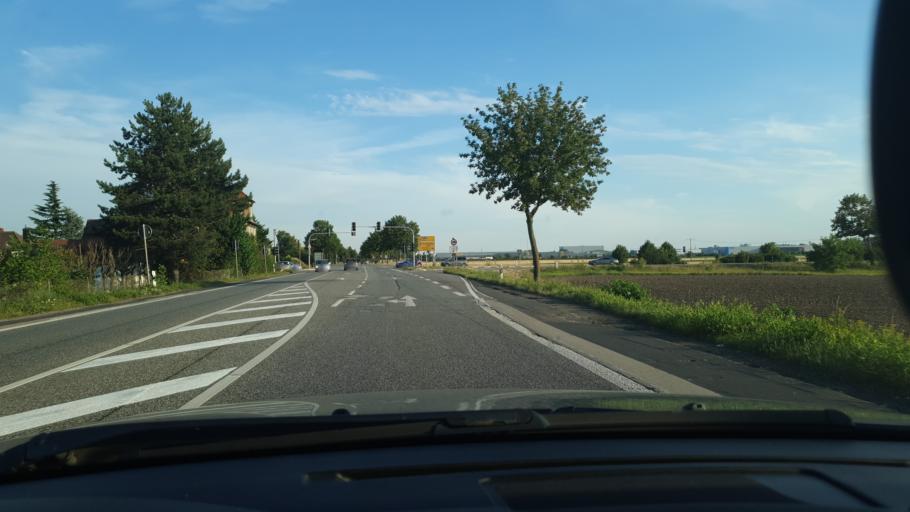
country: DE
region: Rheinland-Pfalz
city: Osthofen
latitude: 49.7069
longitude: 8.3497
